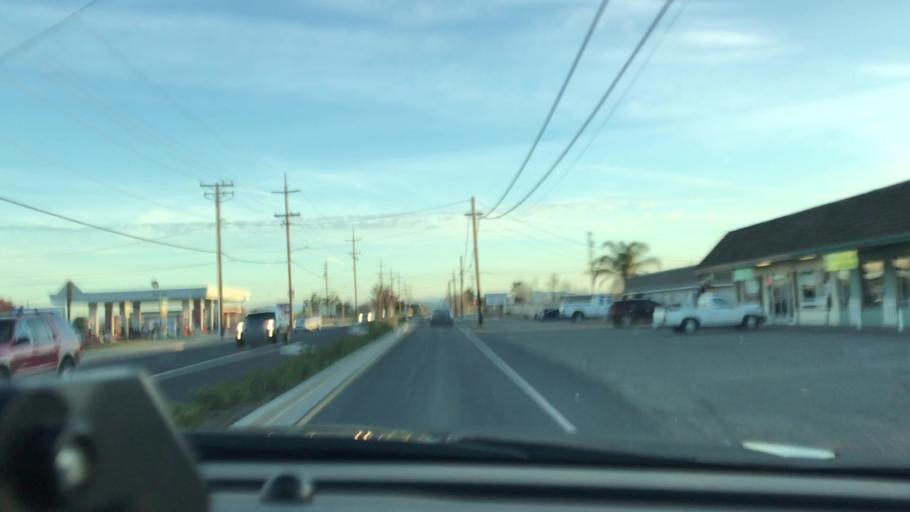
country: US
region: California
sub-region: Contra Costa County
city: Brentwood
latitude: 37.9596
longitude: -121.6962
